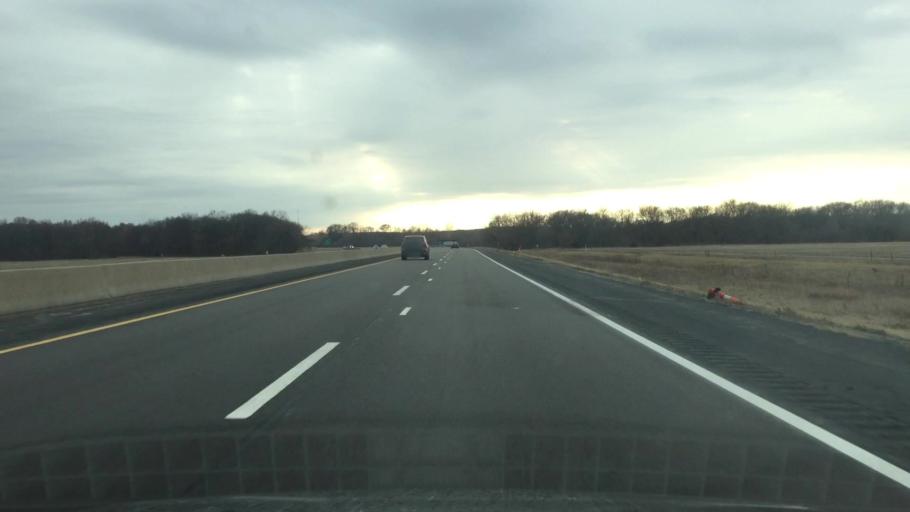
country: US
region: Kansas
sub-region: Osage County
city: Osage City
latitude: 38.6700
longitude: -96.0136
